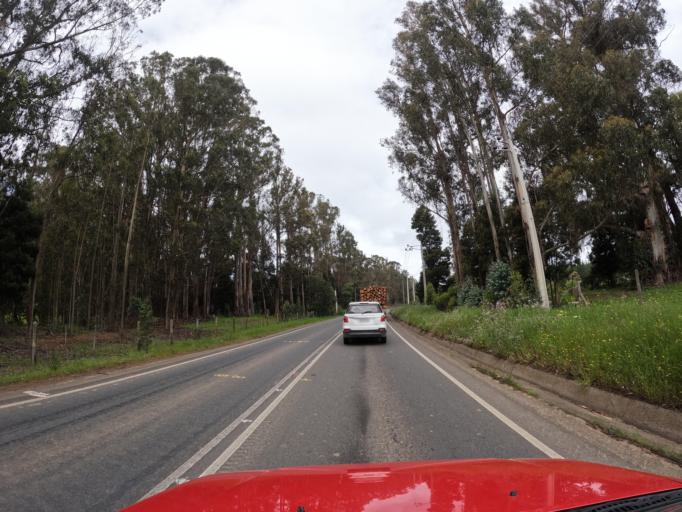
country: CL
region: O'Higgins
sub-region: Provincia de Colchagua
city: Santa Cruz
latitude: -34.3575
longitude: -71.8838
